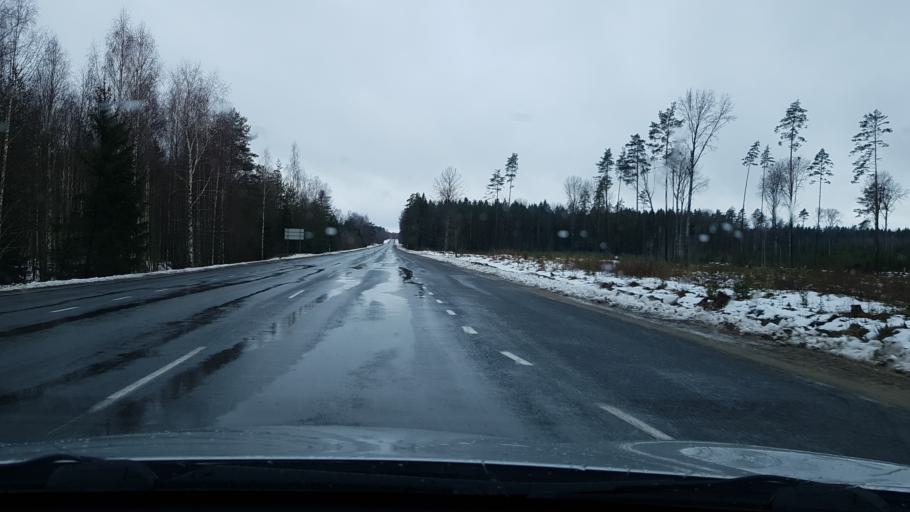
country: LV
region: Apes Novads
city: Ape
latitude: 57.7278
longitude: 26.7801
